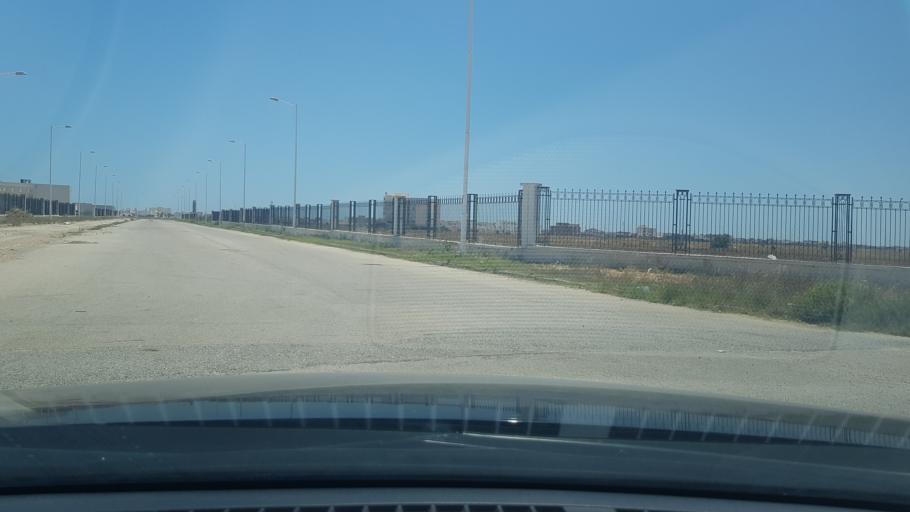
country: TN
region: Safaqis
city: Al Qarmadah
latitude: 34.8383
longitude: 10.7507
